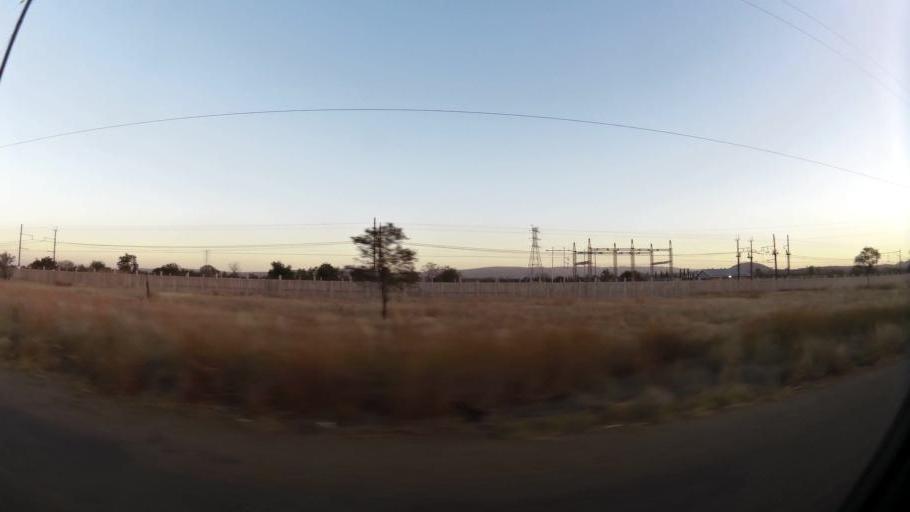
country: ZA
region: North-West
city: Ga-Rankuwa
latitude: -25.6220
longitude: 28.0257
